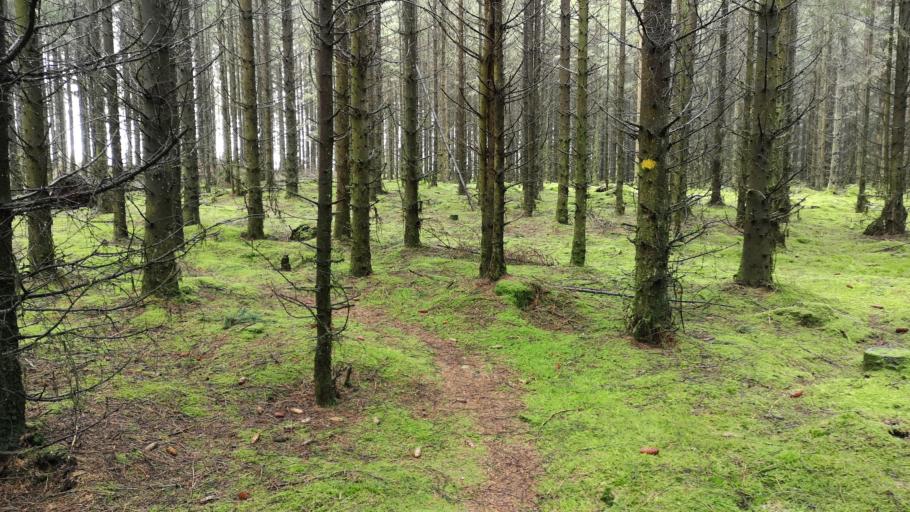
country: DK
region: Central Jutland
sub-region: Ikast-Brande Kommune
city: Brande
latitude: 56.0198
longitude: 9.1612
